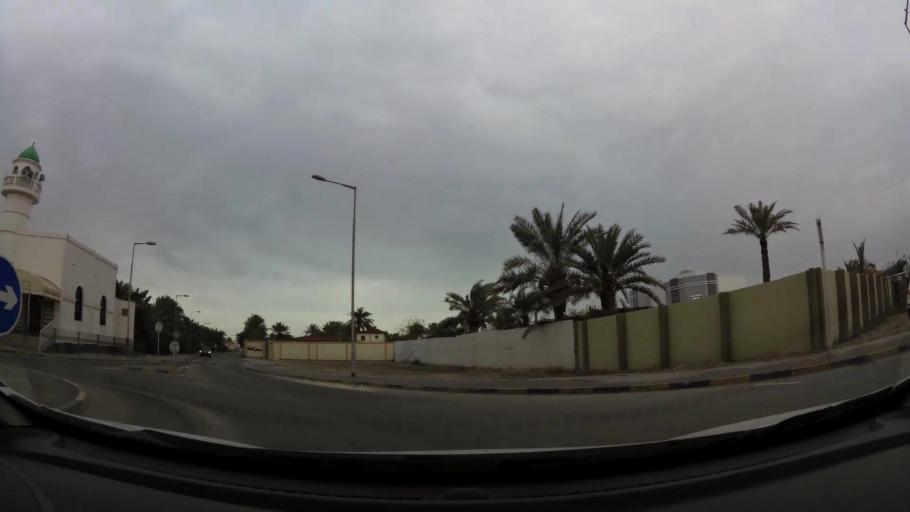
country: BH
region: Central Governorate
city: Madinat Hamad
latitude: 26.1441
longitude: 50.4578
